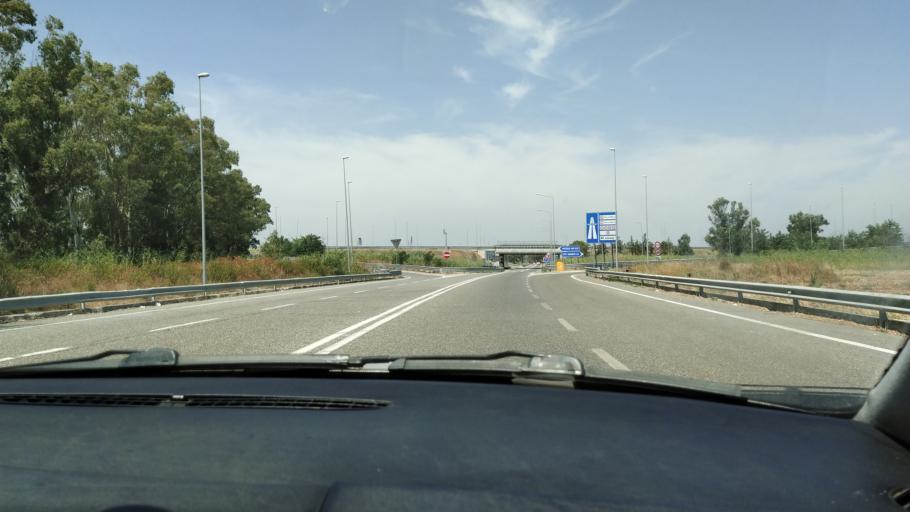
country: IT
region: Apulia
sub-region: Provincia di Taranto
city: Marina di Ginosa
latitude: 40.3764
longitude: 16.7924
